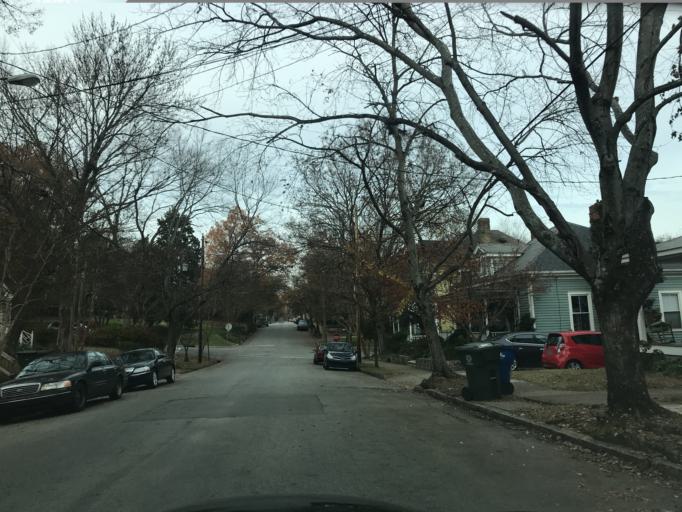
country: US
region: North Carolina
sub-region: Wake County
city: Raleigh
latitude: 35.7874
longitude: -78.6328
